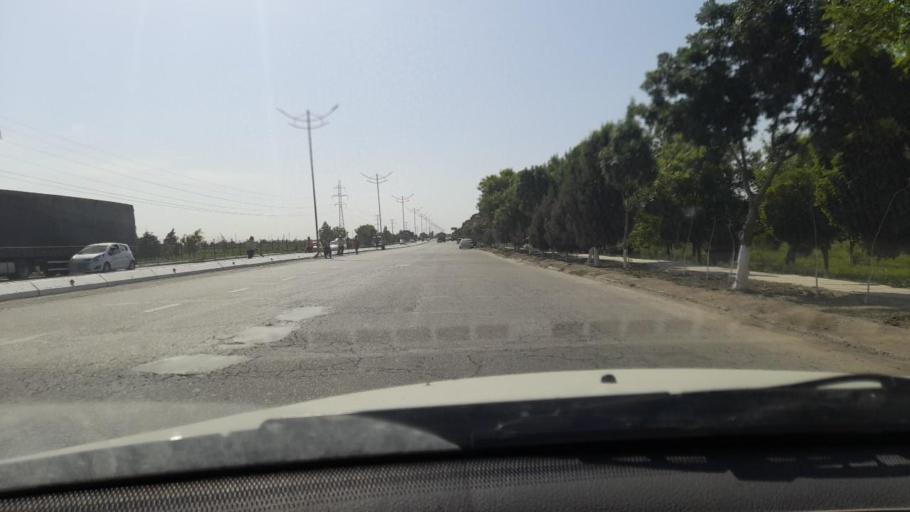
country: UZ
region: Bukhara
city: Bukhara
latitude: 39.8017
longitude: 64.4301
